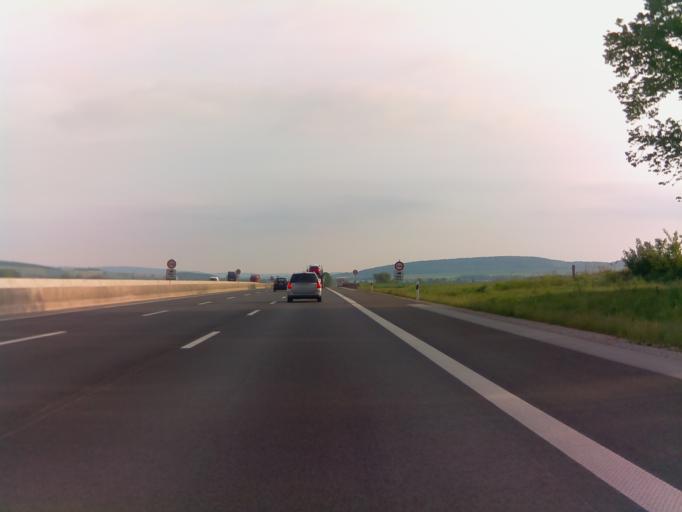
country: DE
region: Lower Saxony
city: Seesen
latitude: 51.9048
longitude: 10.1336
